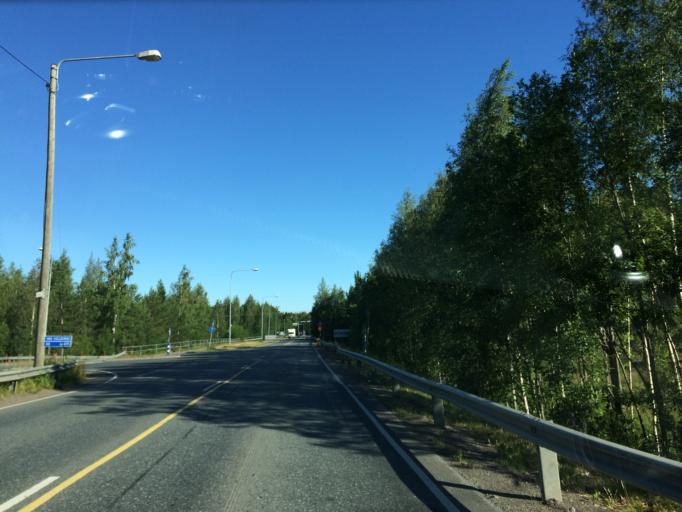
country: FI
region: Haeme
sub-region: Haemeenlinna
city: Haemeenlinna
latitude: 60.9629
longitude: 24.4510
